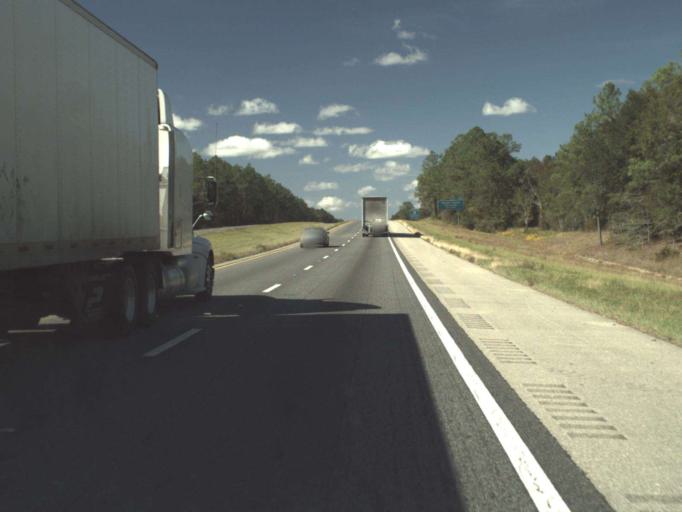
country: US
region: Florida
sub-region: Washington County
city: Chipley
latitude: 30.7466
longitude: -85.5246
